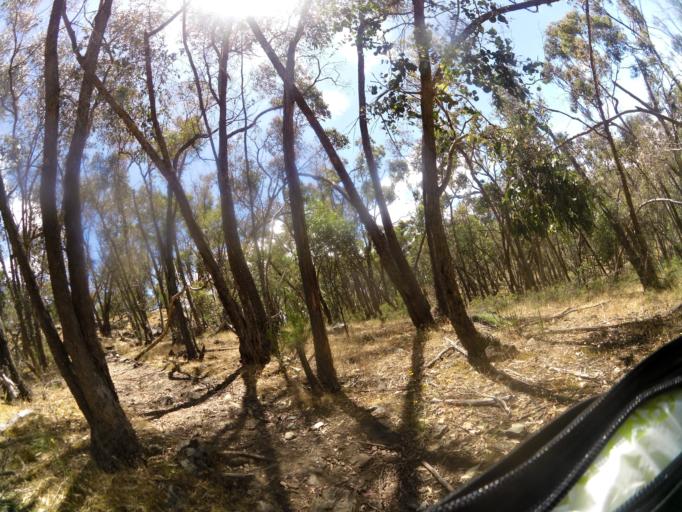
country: AU
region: Victoria
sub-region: Mount Alexander
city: Castlemaine
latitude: -37.0620
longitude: 144.2673
